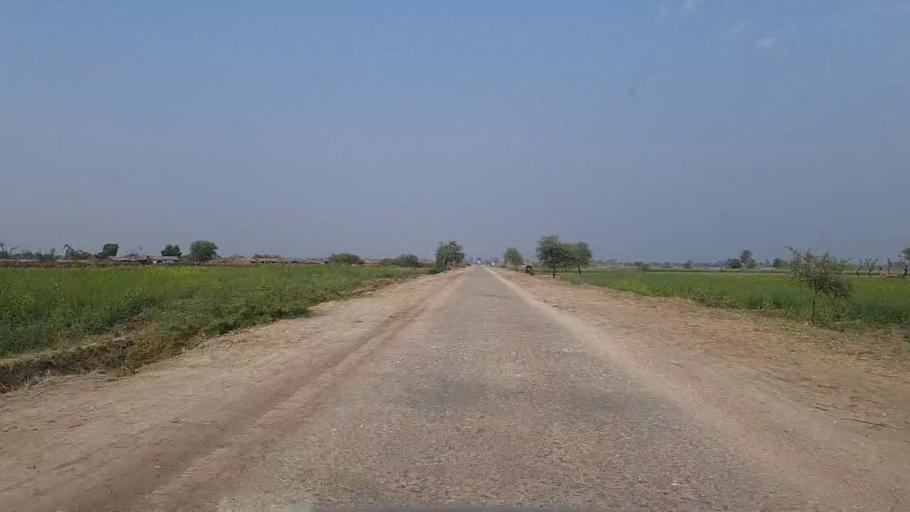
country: PK
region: Sindh
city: Mirwah Gorchani
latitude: 25.4133
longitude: 69.1441
